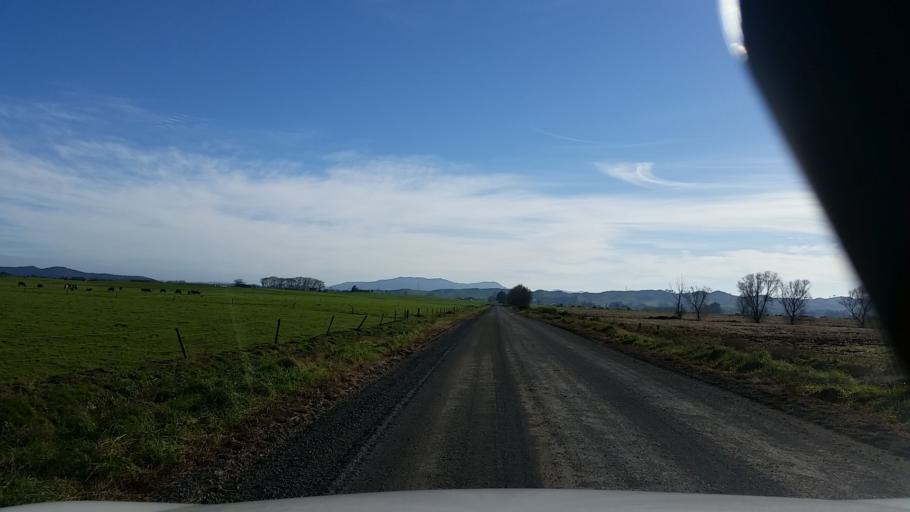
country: NZ
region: Waikato
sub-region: Hamilton City
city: Hamilton
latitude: -37.6324
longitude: 175.4287
